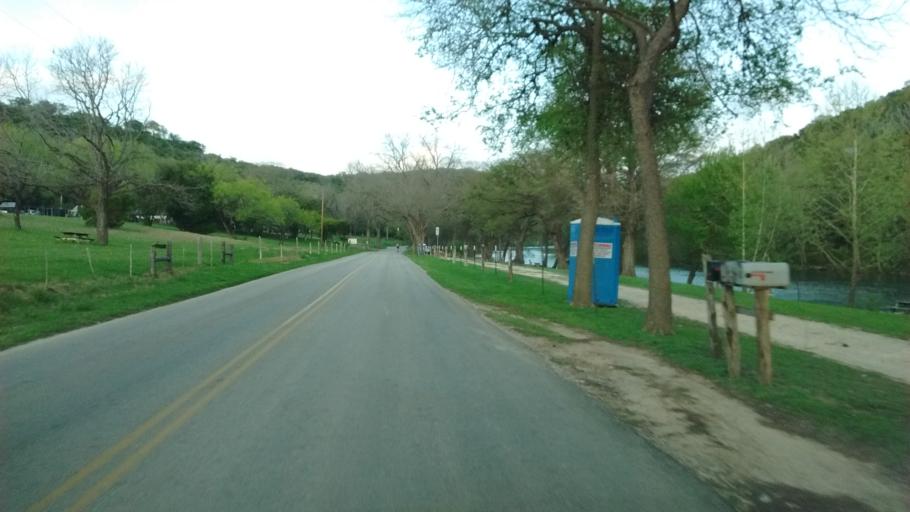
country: US
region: Texas
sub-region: Comal County
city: New Braunfels
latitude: 29.7655
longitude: -98.1518
